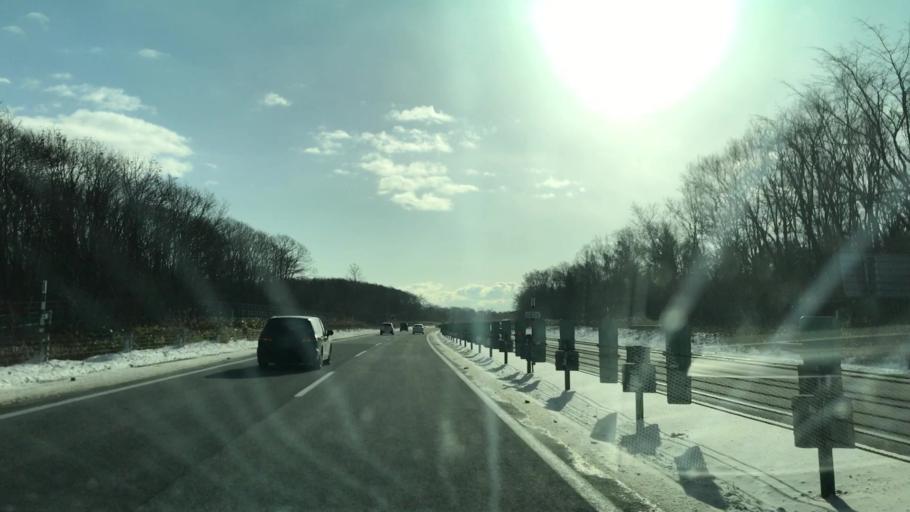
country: JP
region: Hokkaido
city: Chitose
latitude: 42.8345
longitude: 141.6083
